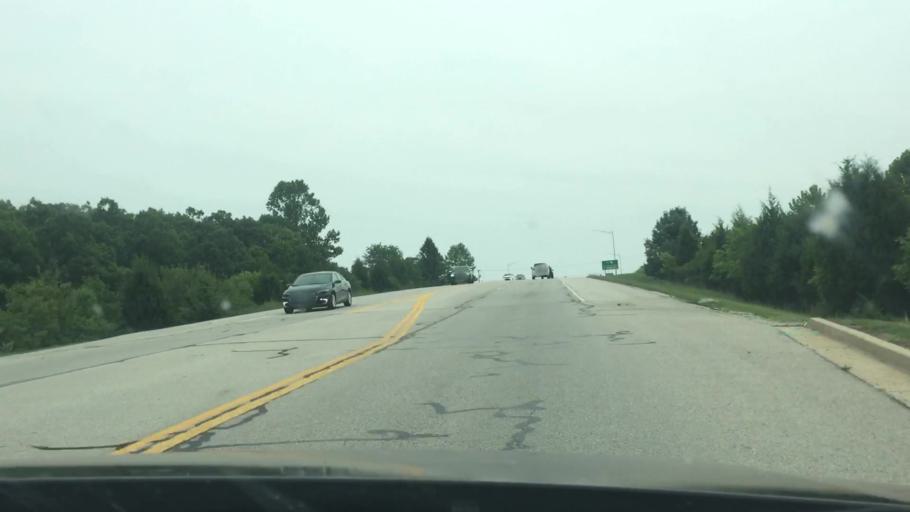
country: US
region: Missouri
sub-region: Miller County
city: Lake Ozark
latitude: 38.1914
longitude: -92.6488
